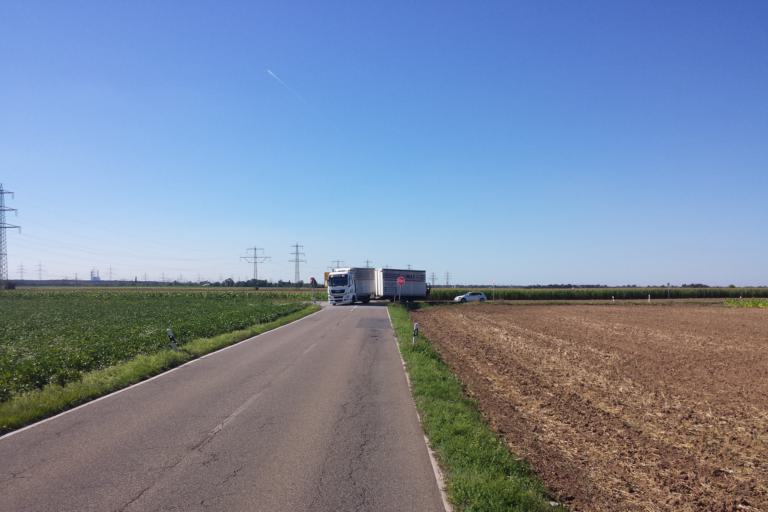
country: DE
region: Baden-Wuerttemberg
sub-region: Karlsruhe Region
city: Eppelheim
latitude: 49.4083
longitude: 8.6154
